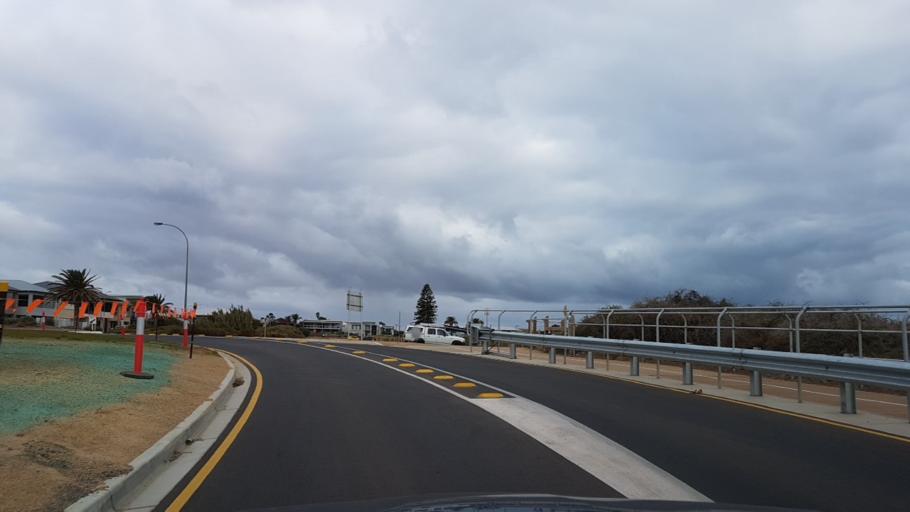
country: AU
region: South Australia
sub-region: Adelaide
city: Port Noarlunga
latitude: -35.1619
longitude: 138.4719
